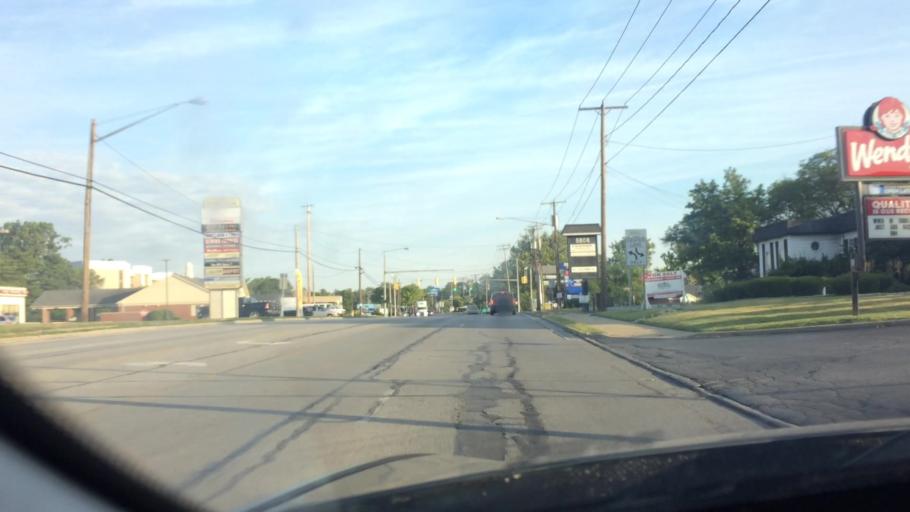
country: US
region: Ohio
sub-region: Lucas County
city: Sylvania
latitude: 41.7113
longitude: -83.6803
